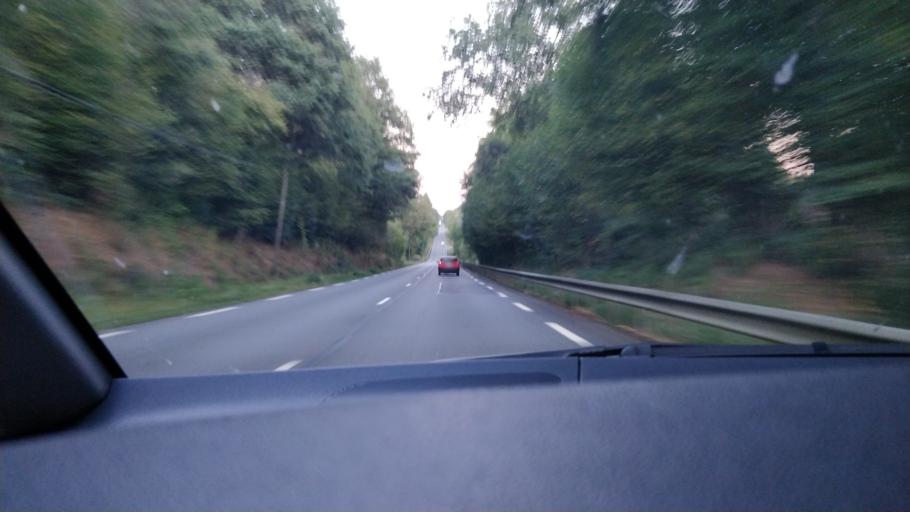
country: FR
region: Poitou-Charentes
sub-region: Departement de la Charente
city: Exideuil
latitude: 45.8783
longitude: 0.6282
